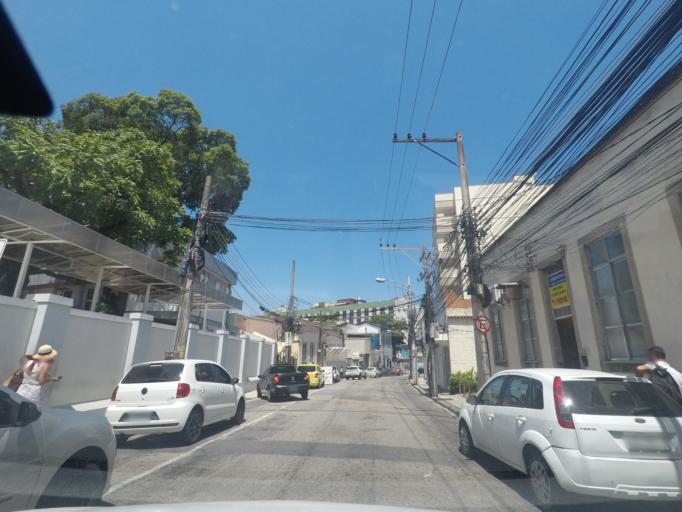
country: BR
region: Rio de Janeiro
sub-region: Rio De Janeiro
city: Rio de Janeiro
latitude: -22.9028
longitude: -43.2194
